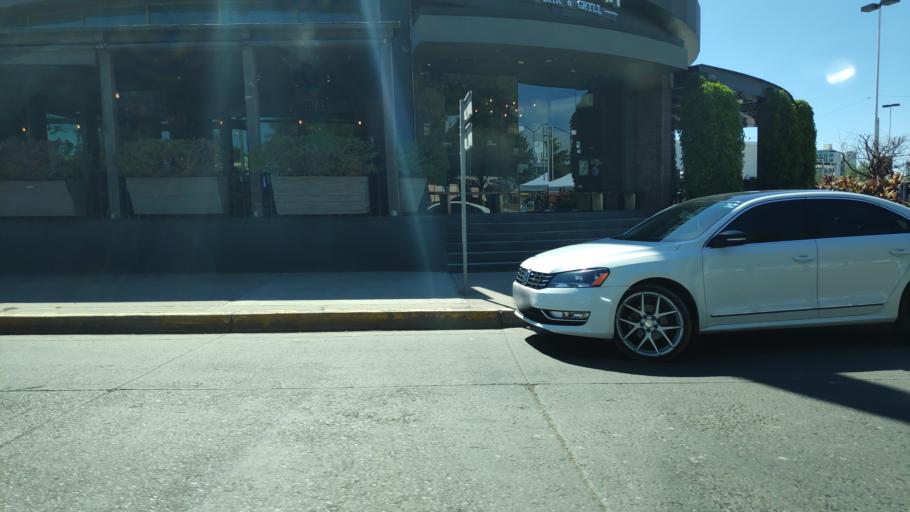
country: MX
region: Sinaloa
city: Culiacan
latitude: 24.8222
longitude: -107.4003
